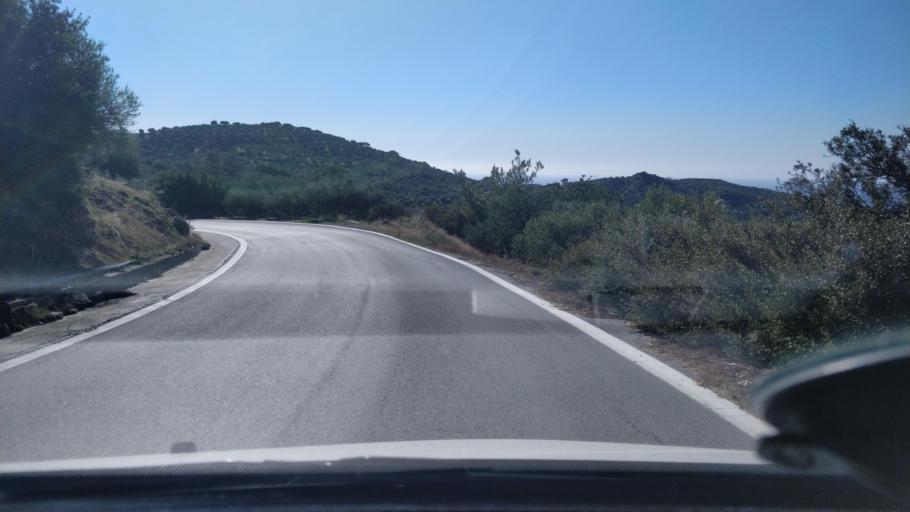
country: GR
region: Crete
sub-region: Nomos Irakleiou
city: Kastelli
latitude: 35.0210
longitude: 25.4481
